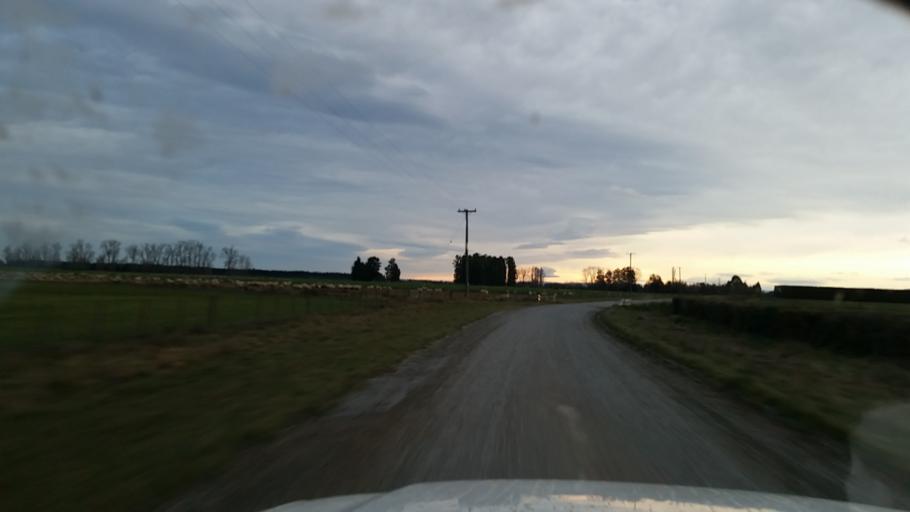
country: NZ
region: Canterbury
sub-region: Ashburton District
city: Ashburton
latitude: -43.8282
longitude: 171.6351
